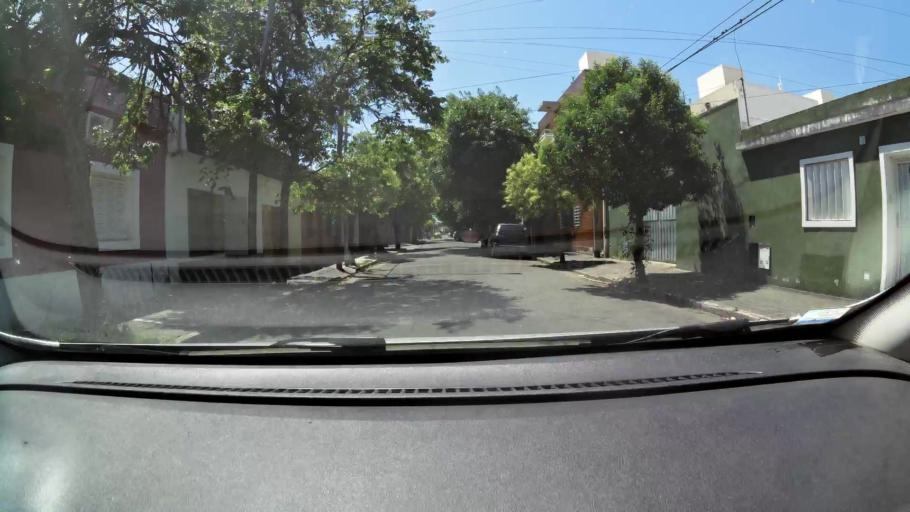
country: AR
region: Cordoba
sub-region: Departamento de Capital
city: Cordoba
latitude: -31.3799
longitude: -64.2036
